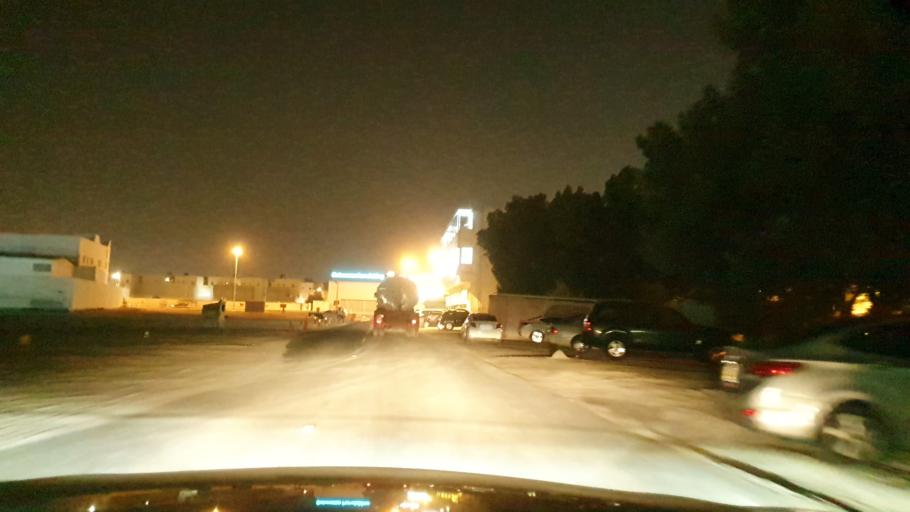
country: BH
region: Manama
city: Jidd Hafs
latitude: 26.2054
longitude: 50.5411
